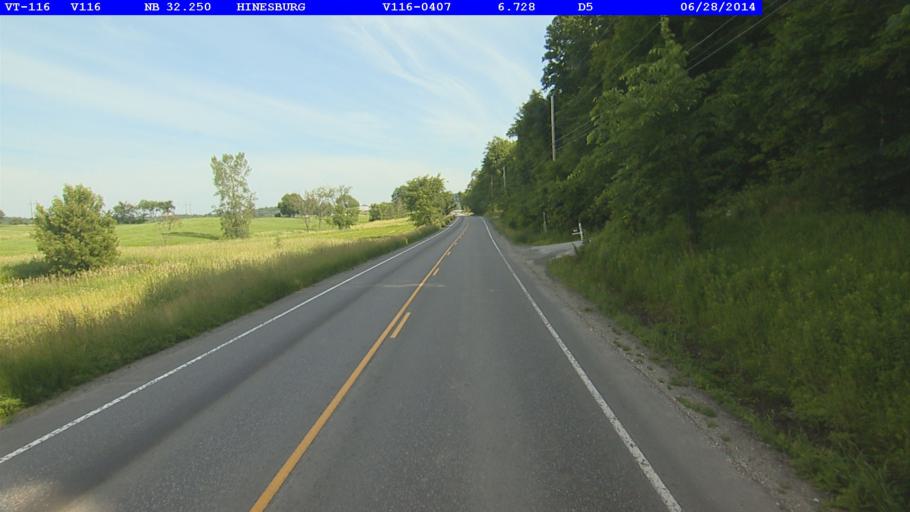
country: US
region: Vermont
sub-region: Chittenden County
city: Hinesburg
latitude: 44.3585
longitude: -73.1228
